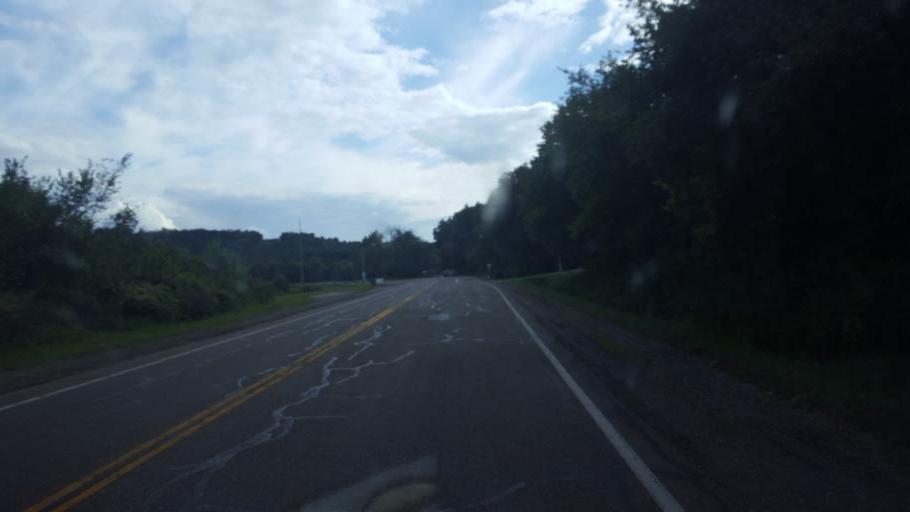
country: US
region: Ohio
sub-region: Tuscarawas County
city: Dover
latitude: 40.5316
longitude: -81.4323
